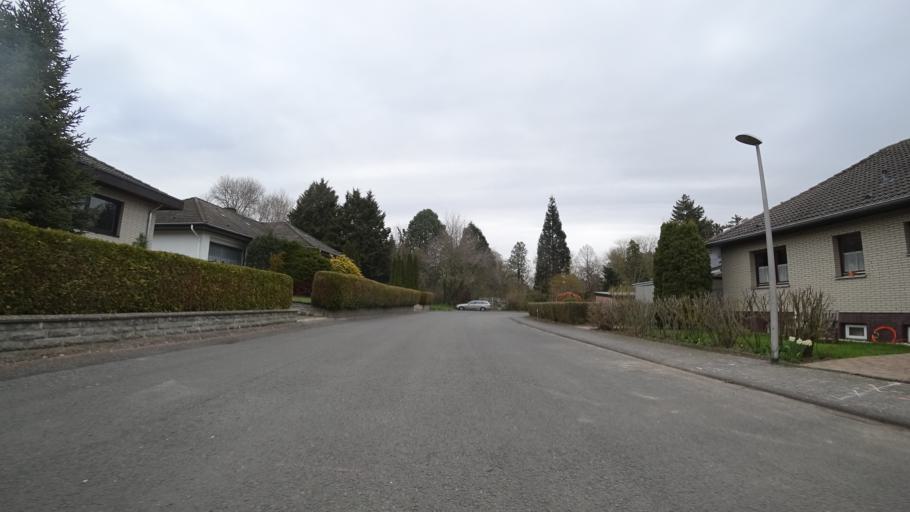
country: DE
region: Hesse
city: Grebenstein
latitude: 51.4264
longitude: 9.4280
